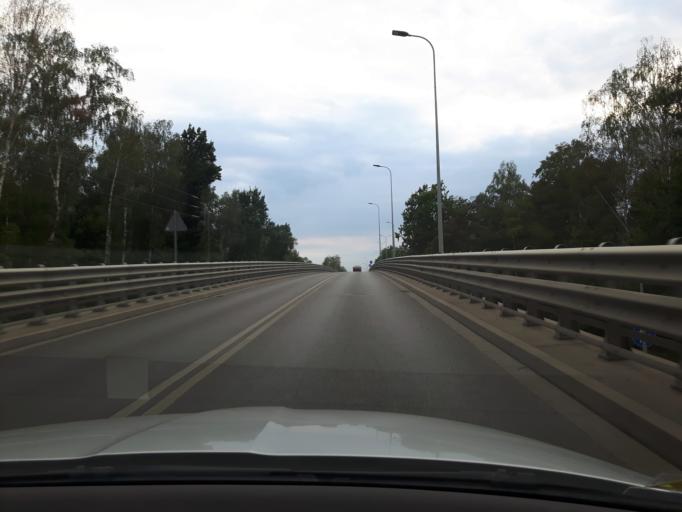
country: PL
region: Masovian Voivodeship
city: Zielonka
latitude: 52.2989
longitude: 21.1489
